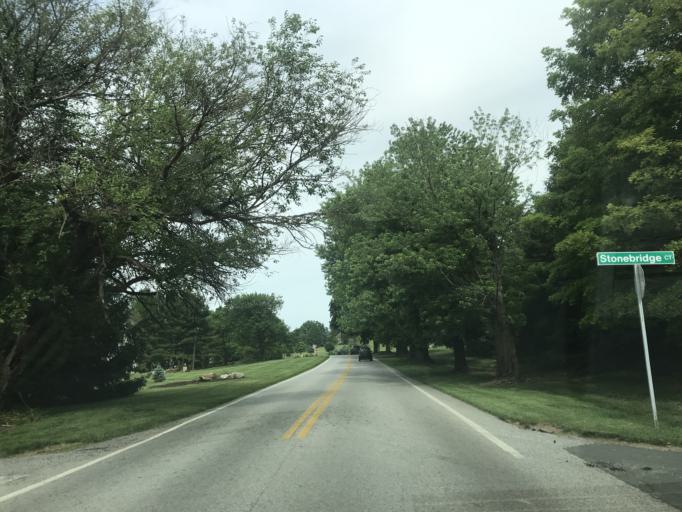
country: US
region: Maryland
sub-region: Baltimore County
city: Hampton
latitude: 39.4253
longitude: -76.5917
